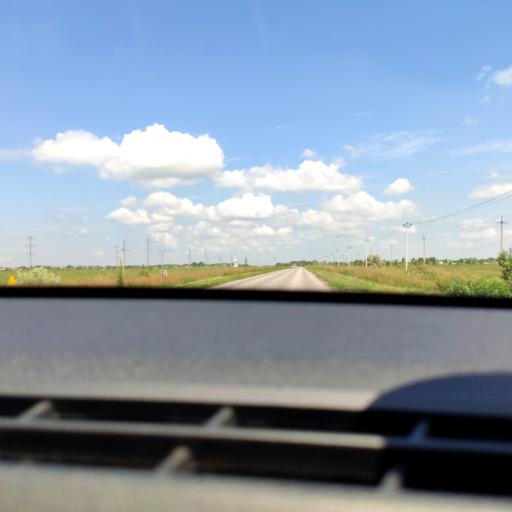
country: RU
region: Samara
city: Podstepki
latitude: 53.5565
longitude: 49.0913
